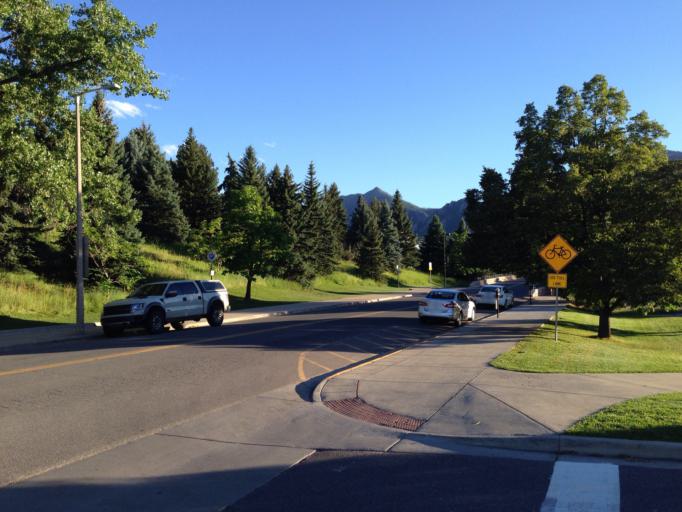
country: US
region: Colorado
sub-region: Boulder County
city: Boulder
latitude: 40.0048
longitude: -105.2626
